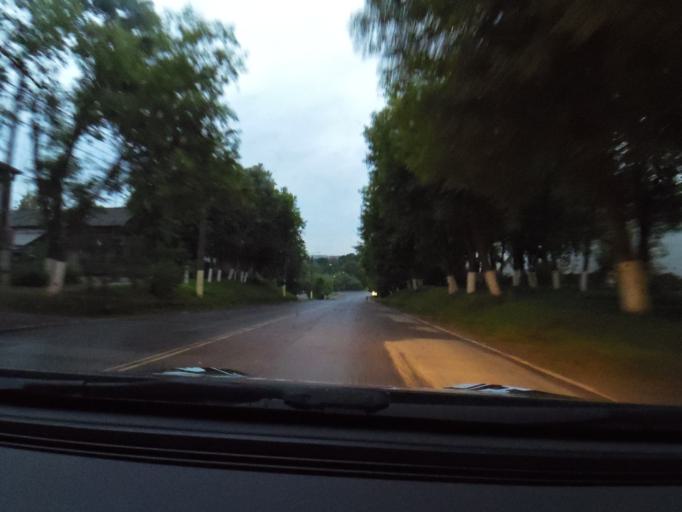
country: RU
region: Vladimir
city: Aleksandrov
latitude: 56.3993
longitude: 38.7408
